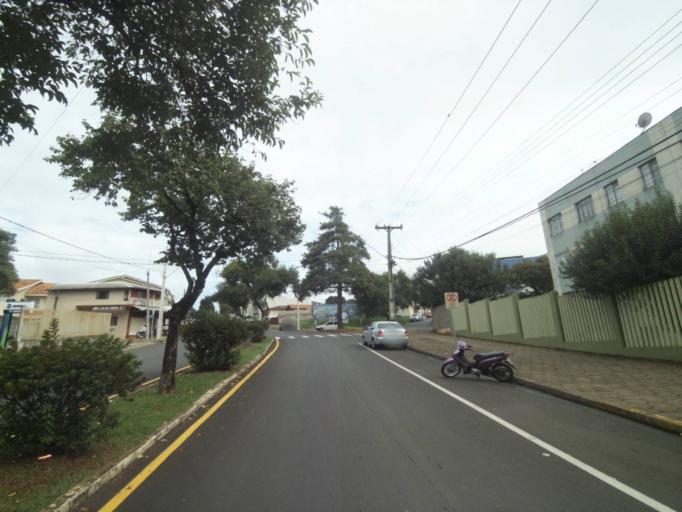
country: BR
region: Parana
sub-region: Telemaco Borba
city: Telemaco Borba
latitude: -24.3335
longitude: -50.6157
